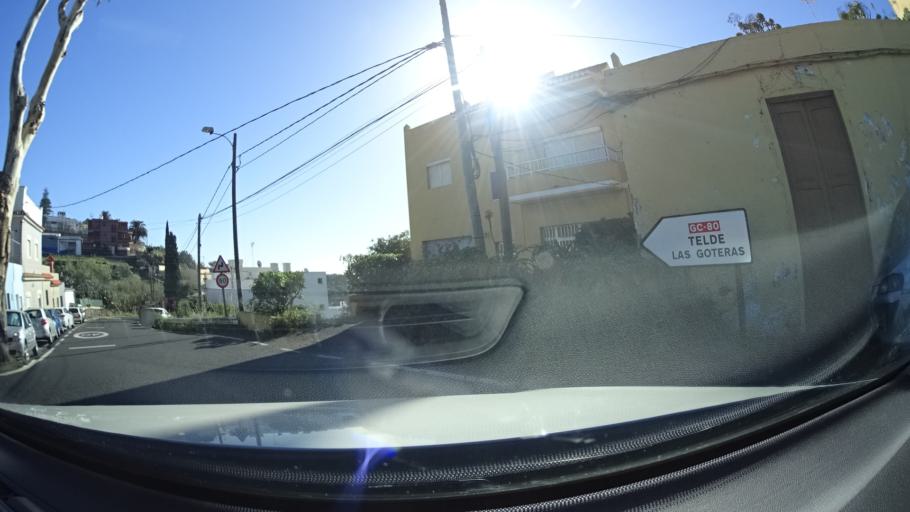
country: ES
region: Canary Islands
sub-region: Provincia de Las Palmas
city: Santa Brigida
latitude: 28.0277
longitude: -15.4763
